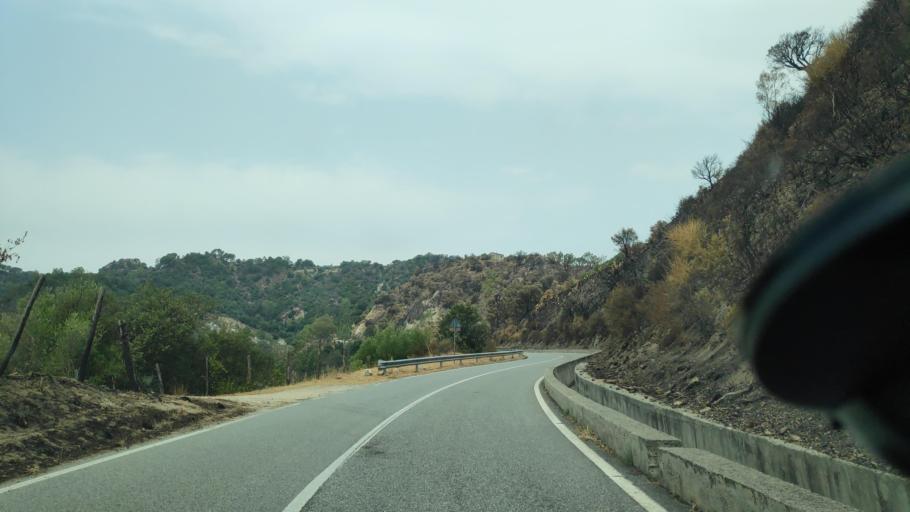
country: IT
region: Calabria
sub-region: Provincia di Catanzaro
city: Sant'Andrea Apostolo dello Ionio
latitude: 38.6402
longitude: 16.5200
